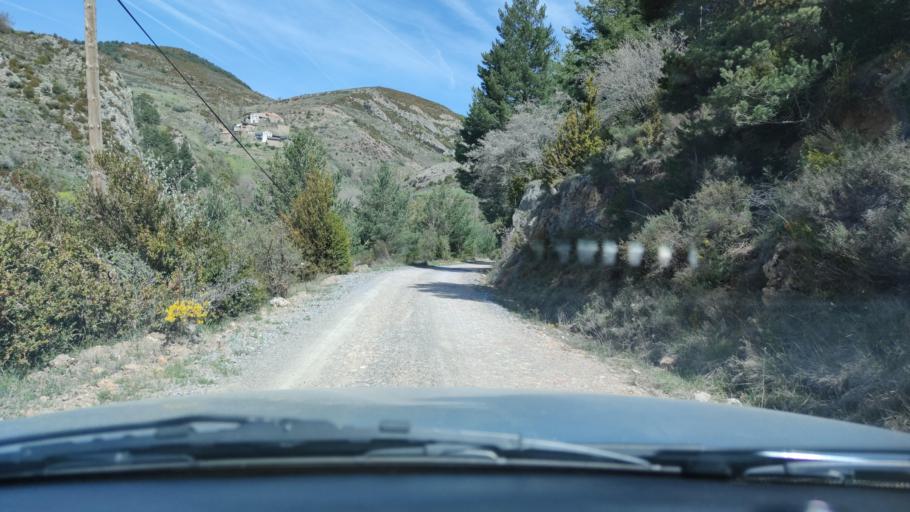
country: ES
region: Catalonia
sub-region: Provincia de Lleida
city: Sort
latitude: 42.2931
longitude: 1.1821
